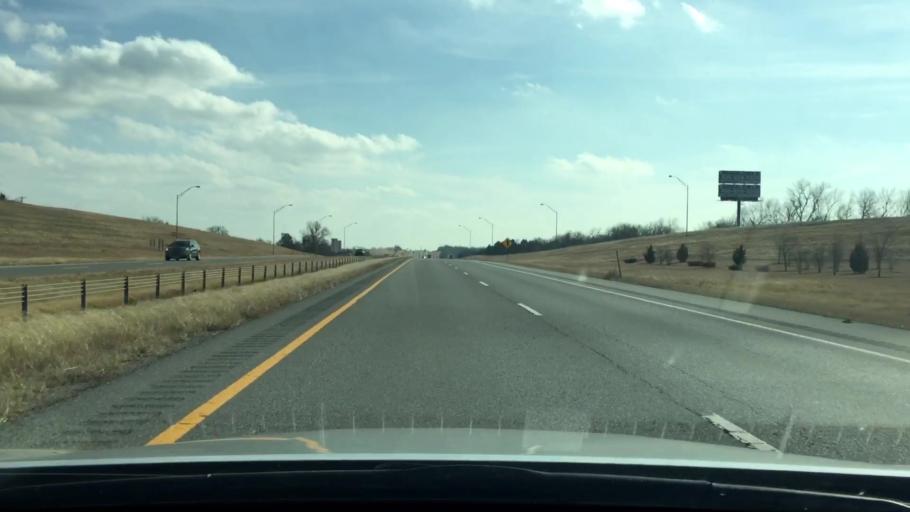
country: US
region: Oklahoma
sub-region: McClain County
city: Purcell
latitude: 34.9819
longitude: -97.3726
